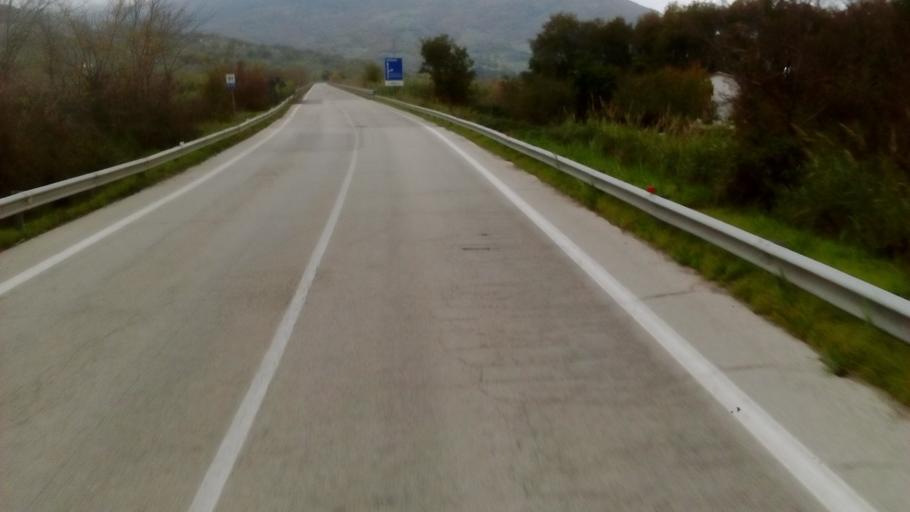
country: IT
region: Abruzzo
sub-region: Provincia di Chieti
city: Celenza sul Trigno
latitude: 41.8737
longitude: 14.6036
